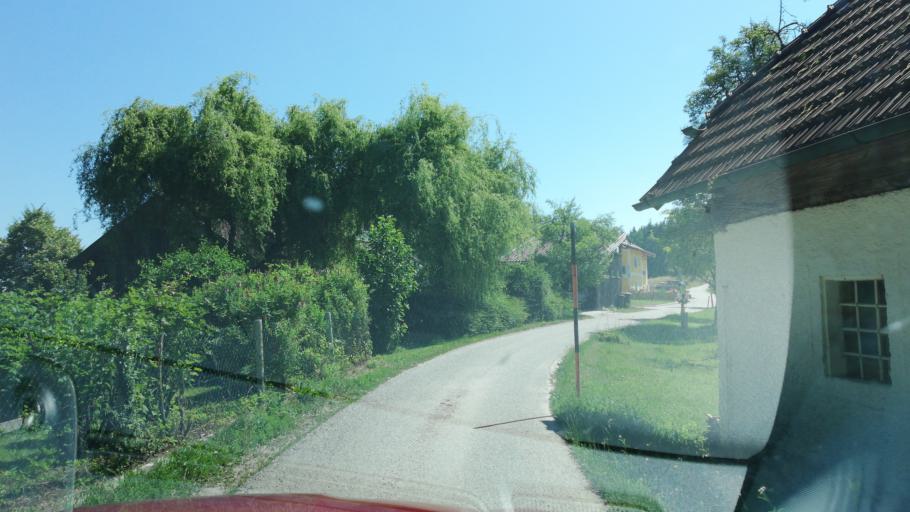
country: AT
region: Upper Austria
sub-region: Wels-Land
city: Gunskirchen
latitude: 48.1827
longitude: 13.9452
